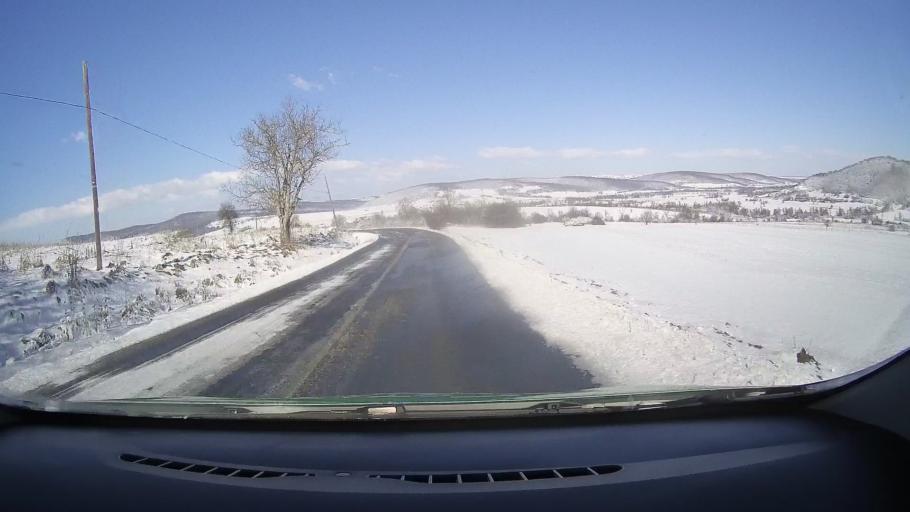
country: RO
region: Sibiu
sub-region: Comuna Rosia
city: Rosia
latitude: 45.7990
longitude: 24.3856
